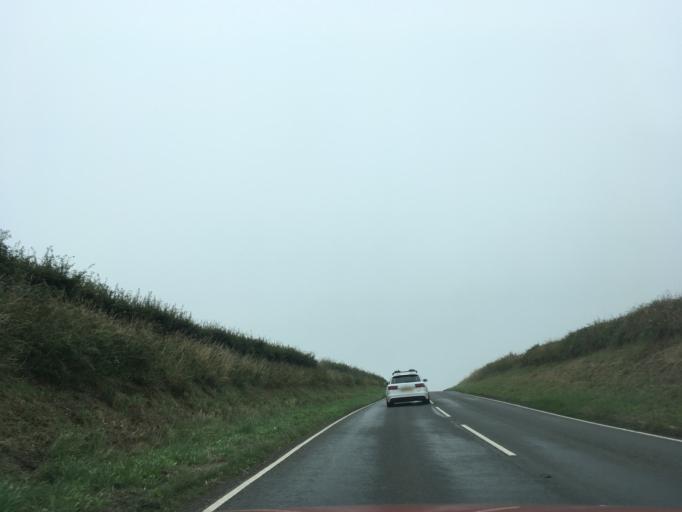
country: GB
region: Wales
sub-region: Pembrokeshire
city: Llanrhian
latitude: 51.8733
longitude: -5.1586
